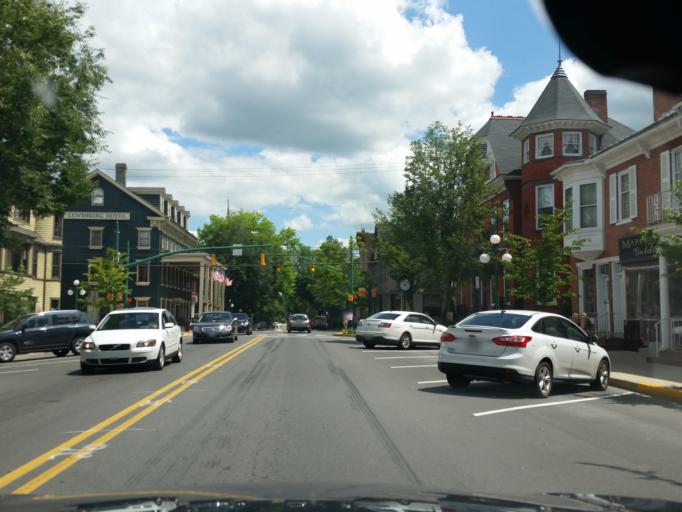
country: US
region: Pennsylvania
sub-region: Union County
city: Lewisburg
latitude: 40.9647
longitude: -76.8842
